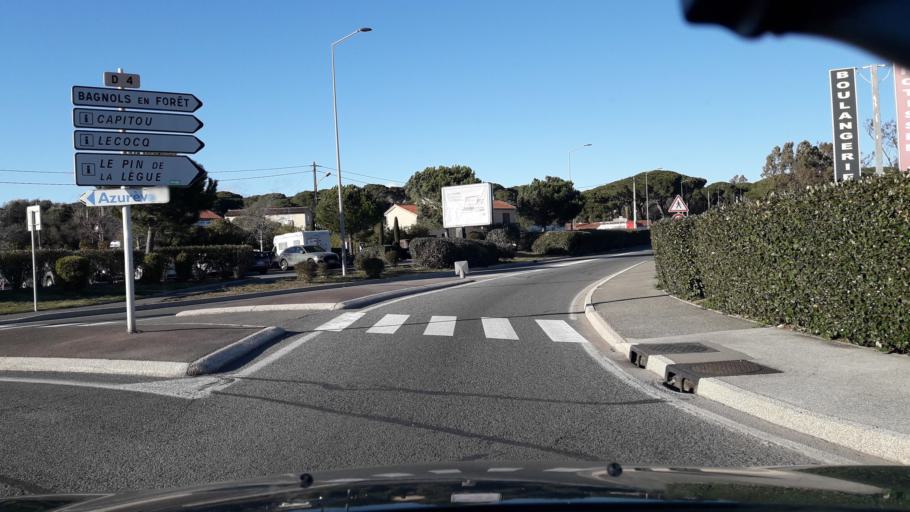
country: FR
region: Provence-Alpes-Cote d'Azur
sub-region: Departement du Var
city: Frejus
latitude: 43.4534
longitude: 6.7268
